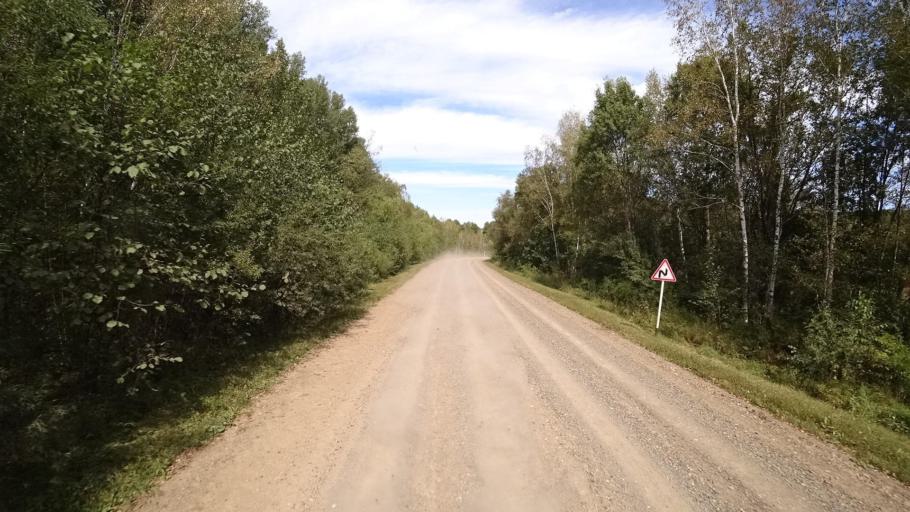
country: RU
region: Primorskiy
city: Yakovlevka
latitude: 44.6761
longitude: 133.6126
